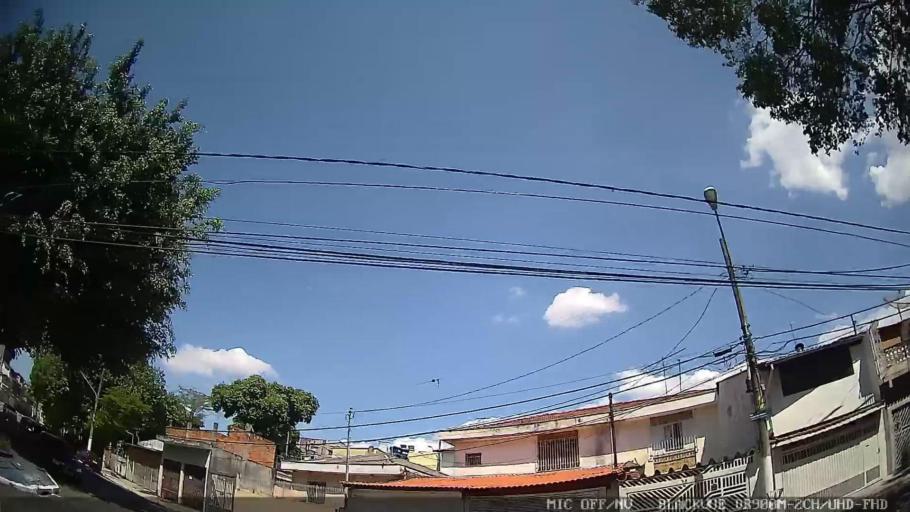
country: BR
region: Sao Paulo
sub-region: Guarulhos
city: Guarulhos
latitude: -23.5004
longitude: -46.4979
